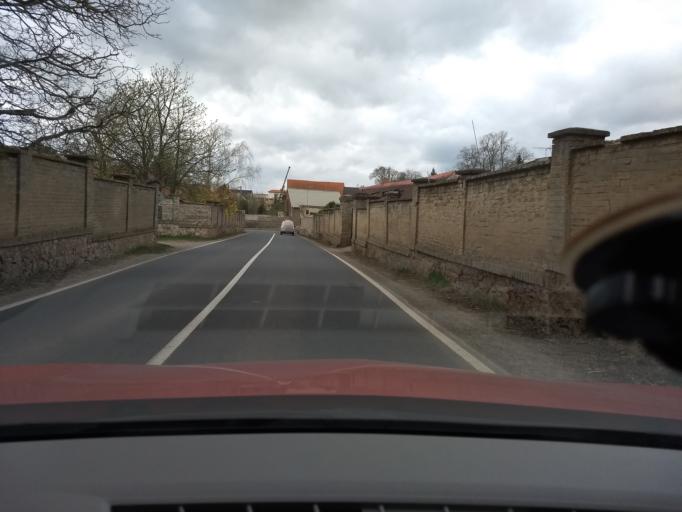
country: CZ
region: Central Bohemia
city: Unhost'
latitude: 50.0535
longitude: 14.1664
